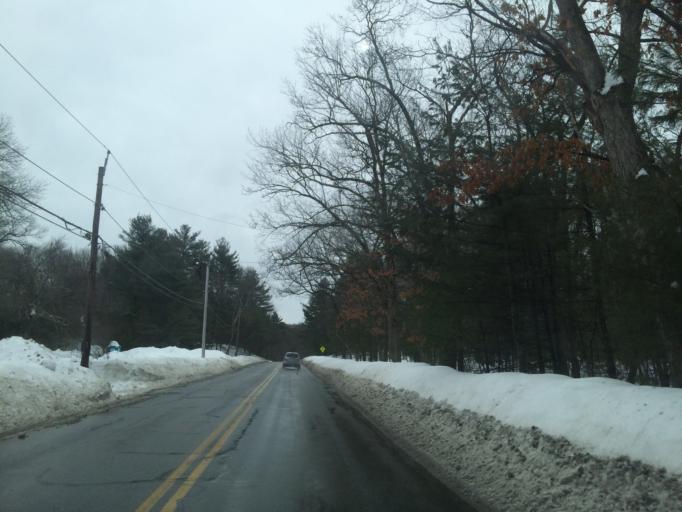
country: US
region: Massachusetts
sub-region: Middlesex County
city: Concord
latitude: 42.4422
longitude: -71.3377
